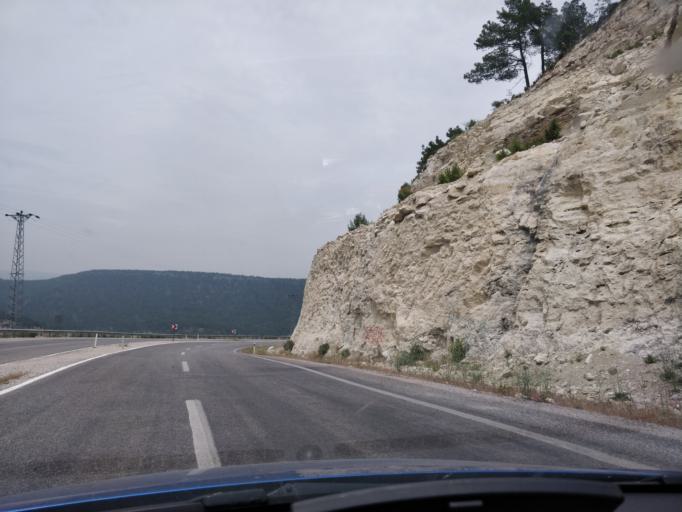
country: TR
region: Mersin
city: Tasucu
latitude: 36.3926
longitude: 33.8409
